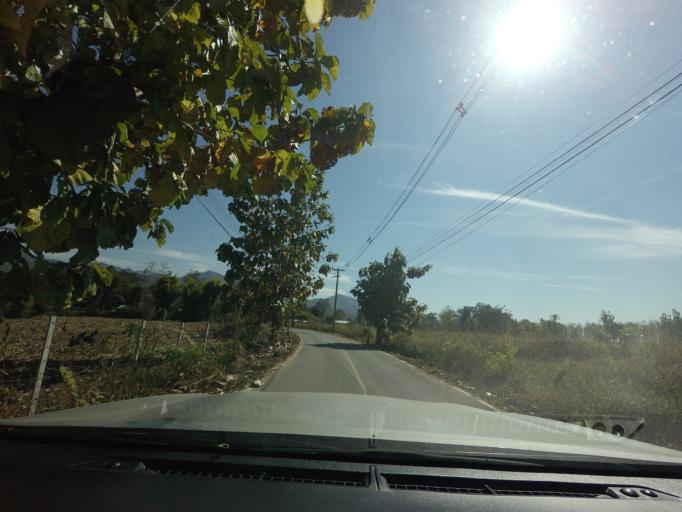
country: TH
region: Mae Hong Son
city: Wiang Nuea
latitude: 19.3865
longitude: 98.4351
